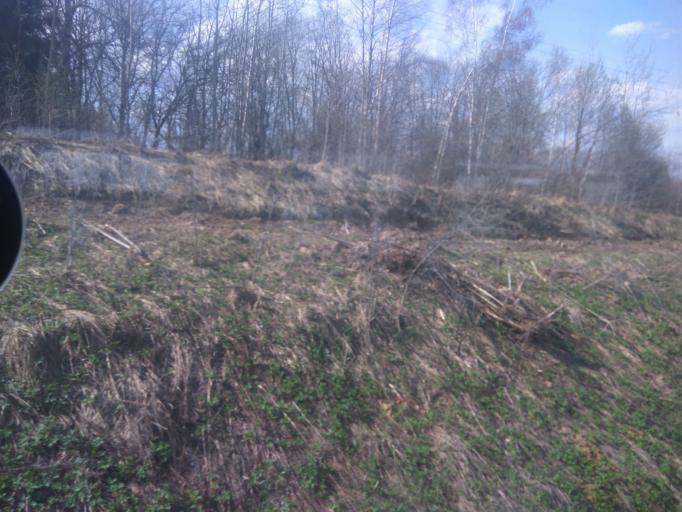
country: RU
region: Moskovskaya
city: Budenovetc
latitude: 56.3131
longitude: 37.7001
